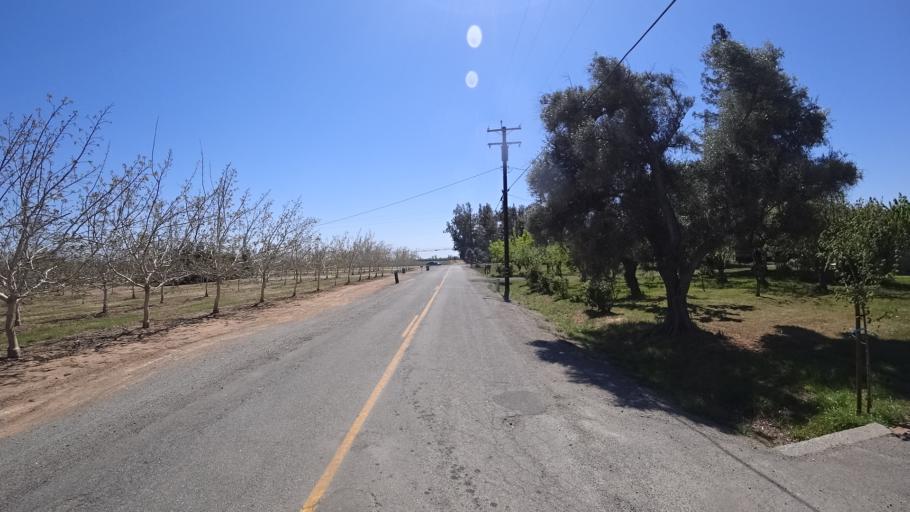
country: US
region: California
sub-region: Glenn County
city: Orland
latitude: 39.7700
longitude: -122.1783
